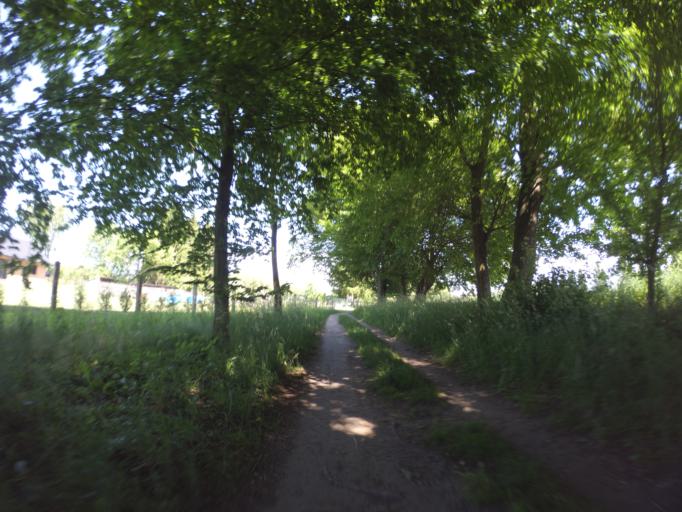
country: CZ
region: Central Bohemia
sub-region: Okres Nymburk
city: Sadska
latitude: 50.1705
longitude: 14.9890
